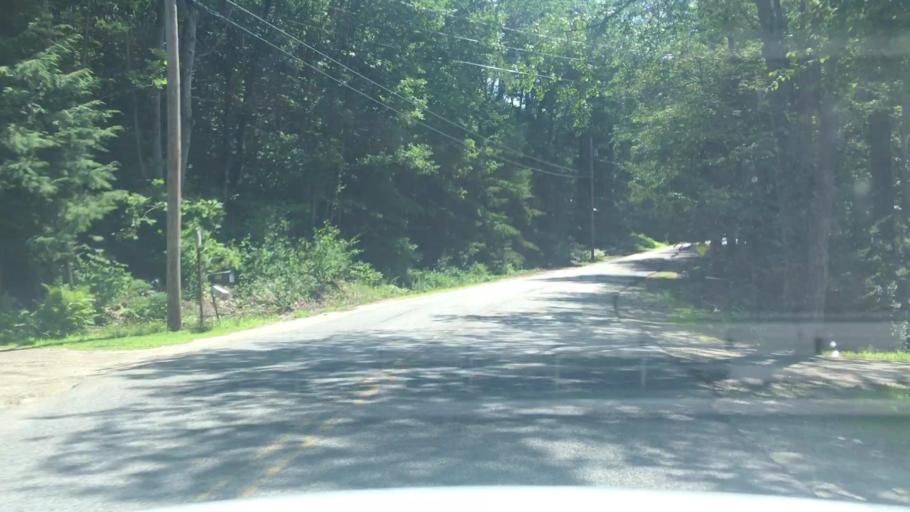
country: US
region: Maine
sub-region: Cumberland County
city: Cumberland Center
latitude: 43.8504
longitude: -70.3144
